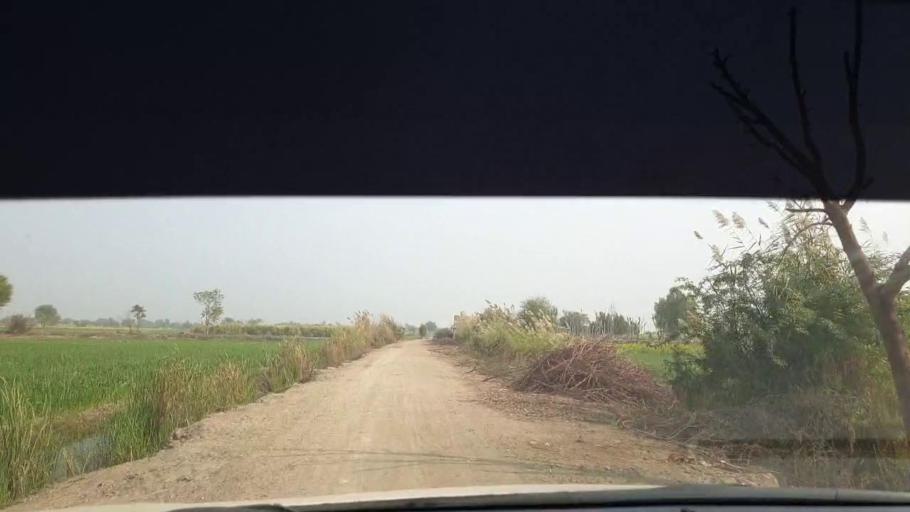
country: PK
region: Sindh
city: Berani
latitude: 25.8420
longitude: 68.8487
